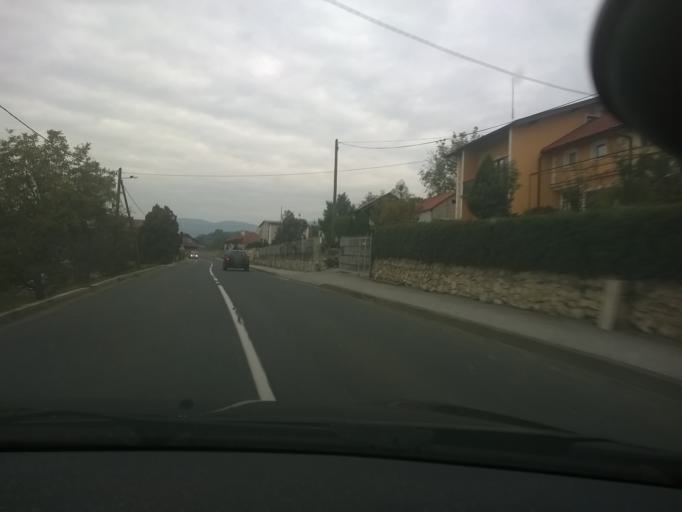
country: HR
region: Krapinsko-Zagorska
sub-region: Grad Krapina
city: Krapina
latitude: 46.1225
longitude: 15.8945
